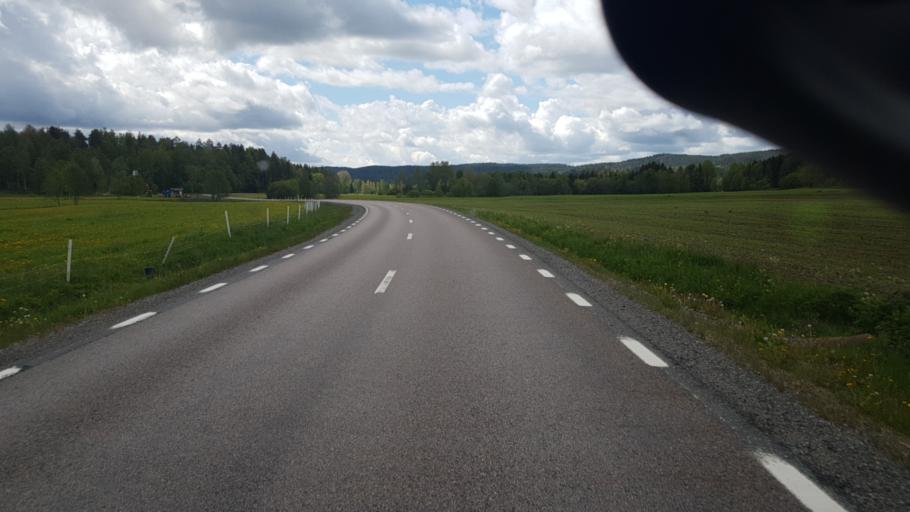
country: SE
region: Vaermland
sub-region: Arjangs Kommun
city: Arjaeng
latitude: 59.6465
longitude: 12.1392
